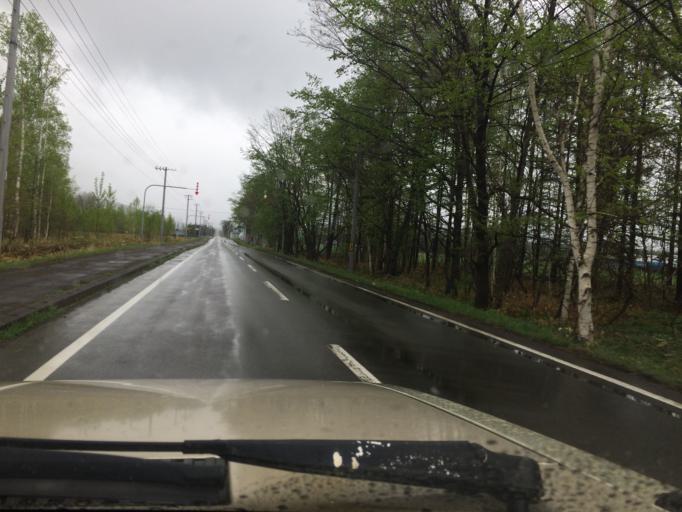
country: JP
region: Hokkaido
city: Obihiro
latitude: 42.8095
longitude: 142.9644
